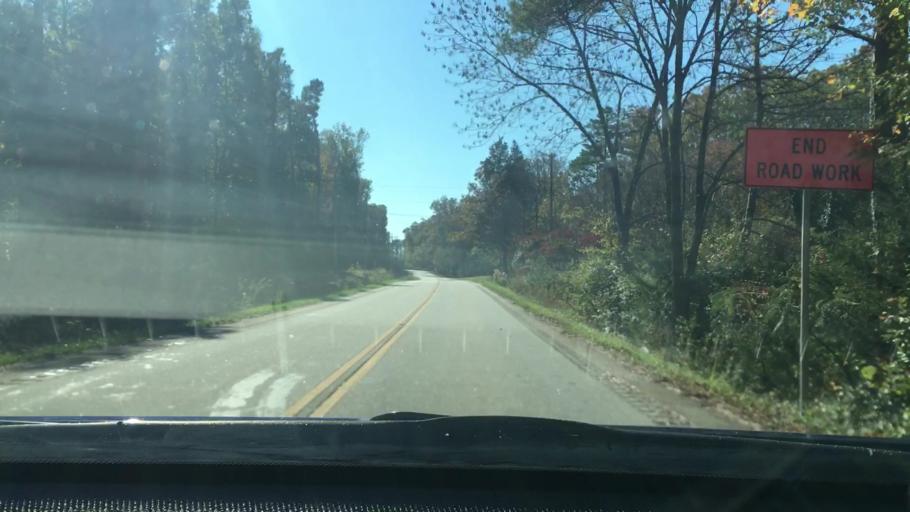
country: US
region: South Carolina
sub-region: Lexington County
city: Irmo
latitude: 34.1291
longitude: -81.1794
